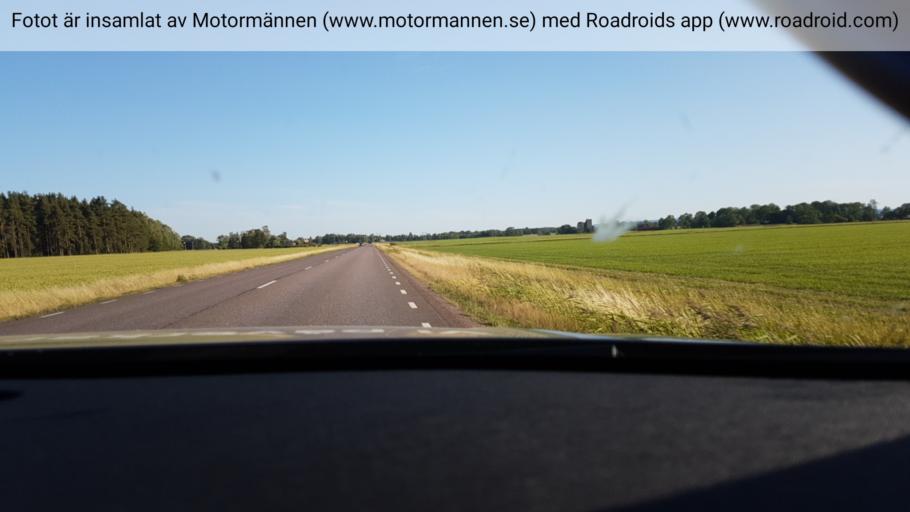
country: SE
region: Vaestra Goetaland
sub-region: Toreboda Kommun
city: Toereboda
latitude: 58.5950
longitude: 14.0088
